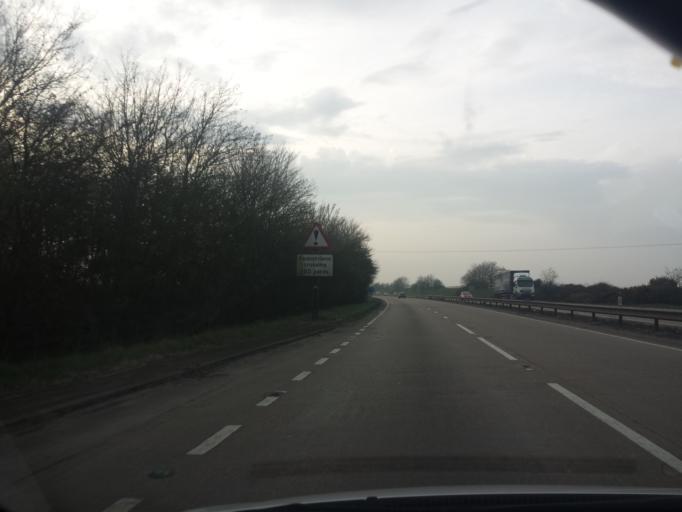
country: GB
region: England
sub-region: Essex
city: Alresford
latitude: 51.8950
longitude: 1.0052
